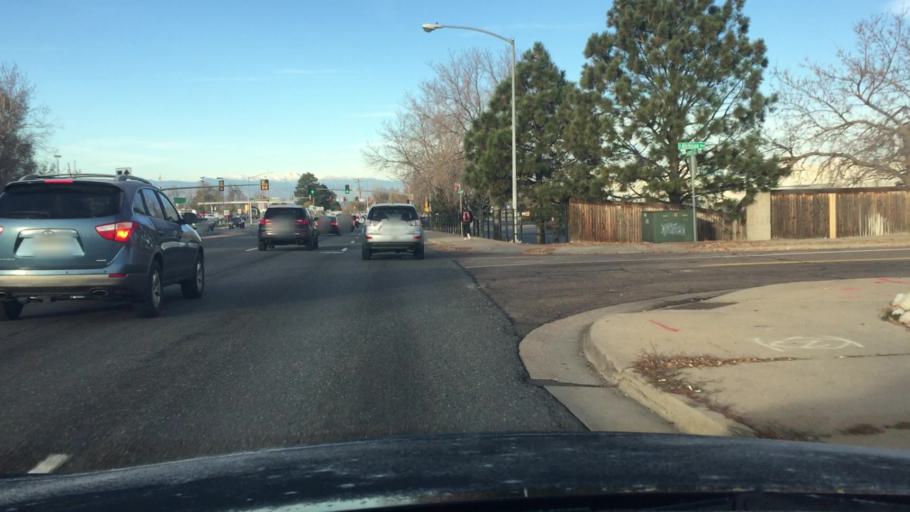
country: US
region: Colorado
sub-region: Arapahoe County
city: Dove Valley
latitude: 39.6387
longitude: -104.8259
